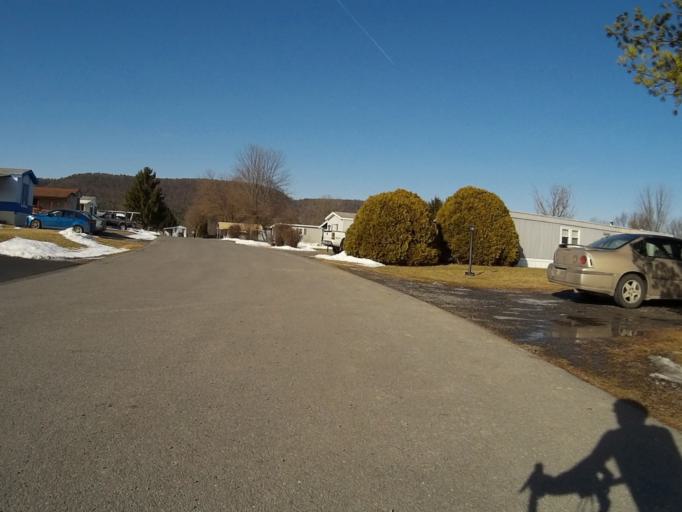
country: US
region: Pennsylvania
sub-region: Centre County
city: Houserville
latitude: 40.8702
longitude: -77.8635
